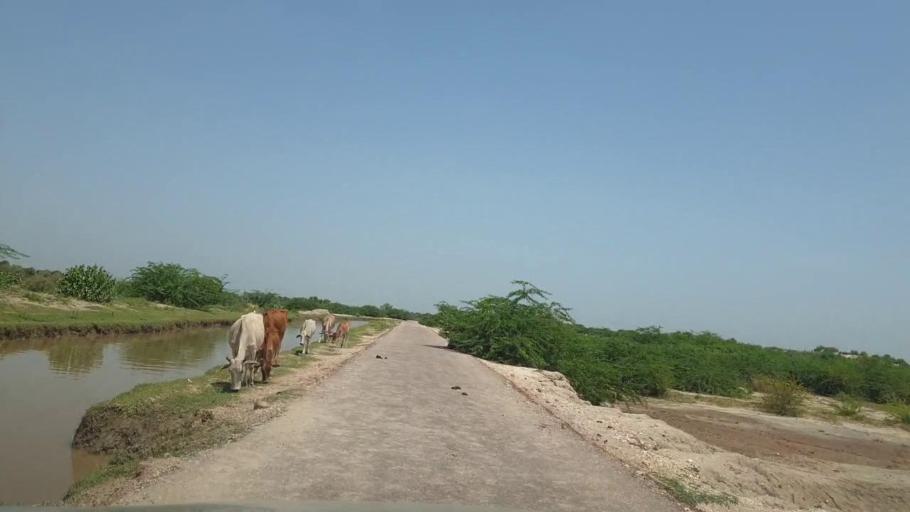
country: PK
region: Sindh
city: Rohri
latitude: 27.6244
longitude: 69.0978
